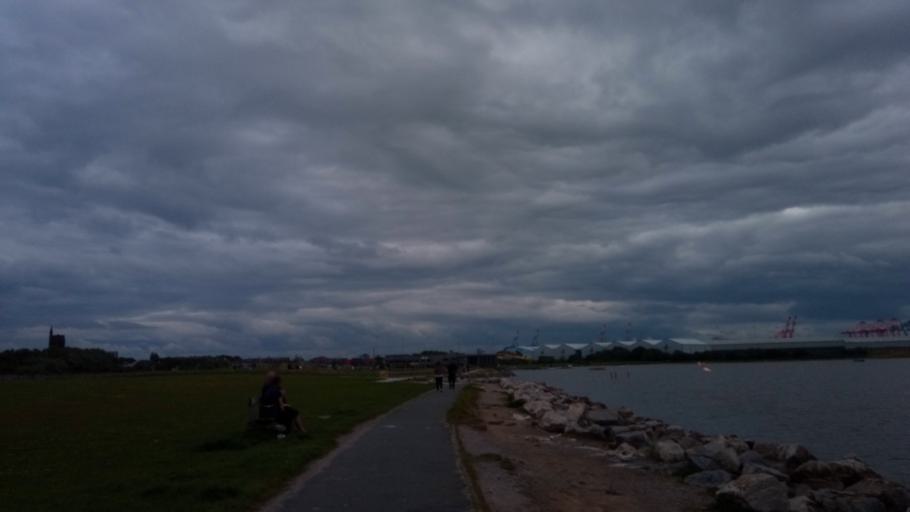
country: GB
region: England
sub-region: Sefton
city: Waterloo
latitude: 53.4728
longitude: -3.0331
